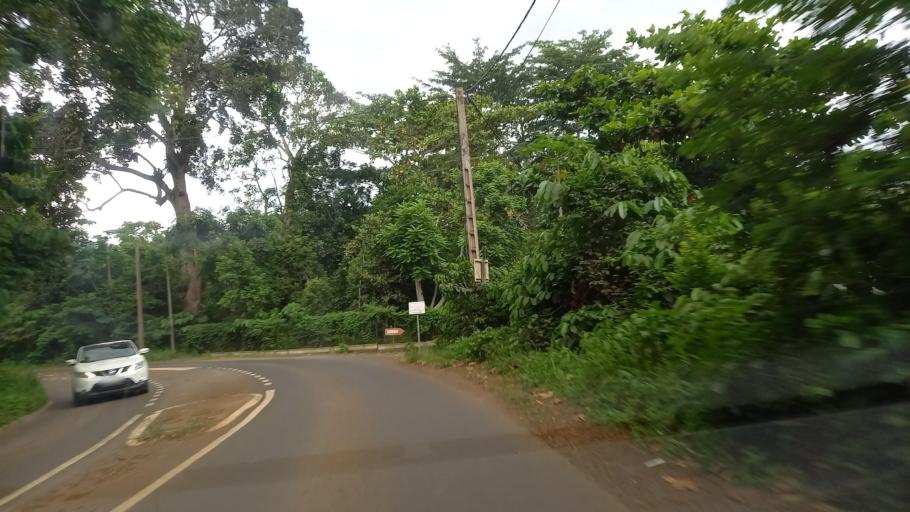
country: YT
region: Ouangani
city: Ouangani
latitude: -12.8313
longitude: 45.1375
